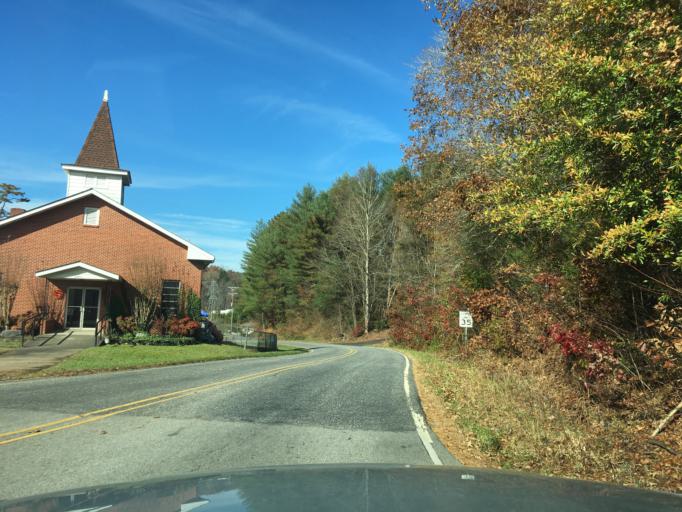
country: US
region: North Carolina
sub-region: Henderson County
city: Etowah
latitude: 35.3046
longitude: -82.6297
